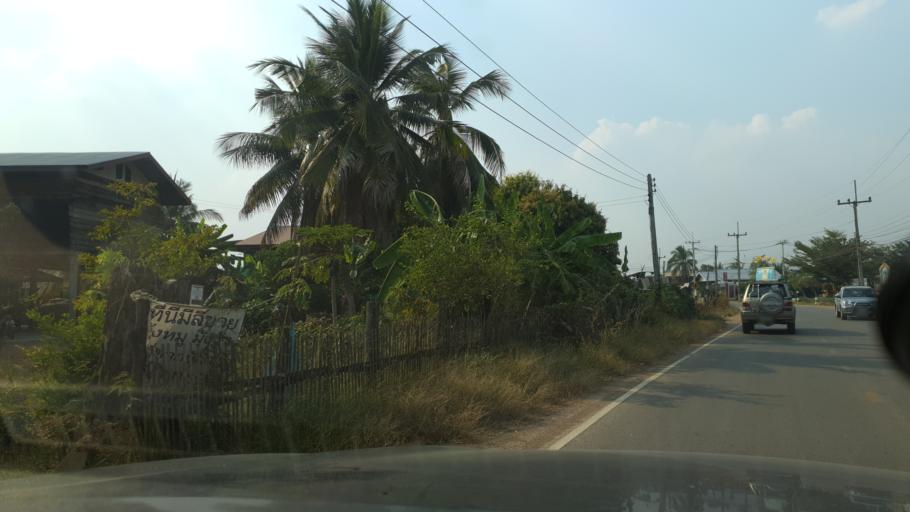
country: TH
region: Sukhothai
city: Ban Dan Lan Hoi
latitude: 17.1137
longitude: 99.5474
